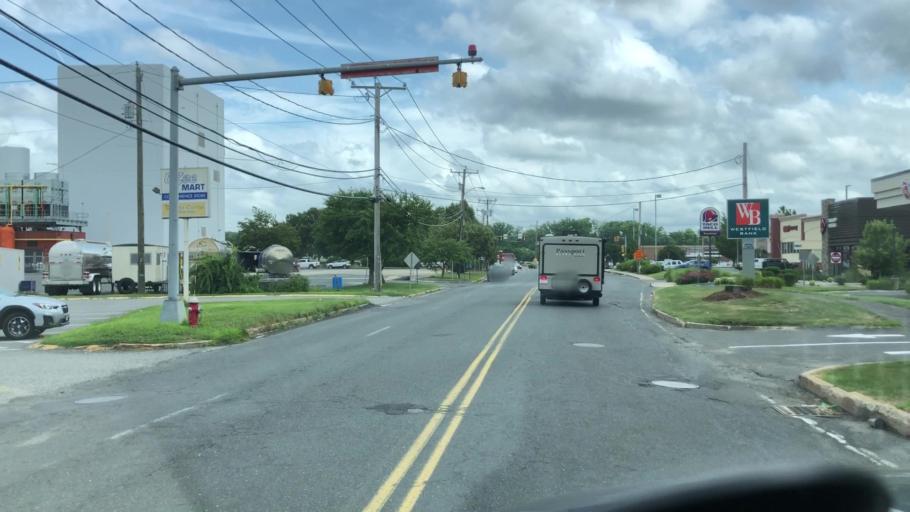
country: US
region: Massachusetts
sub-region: Hampden County
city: West Springfield
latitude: 42.1299
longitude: -72.6286
